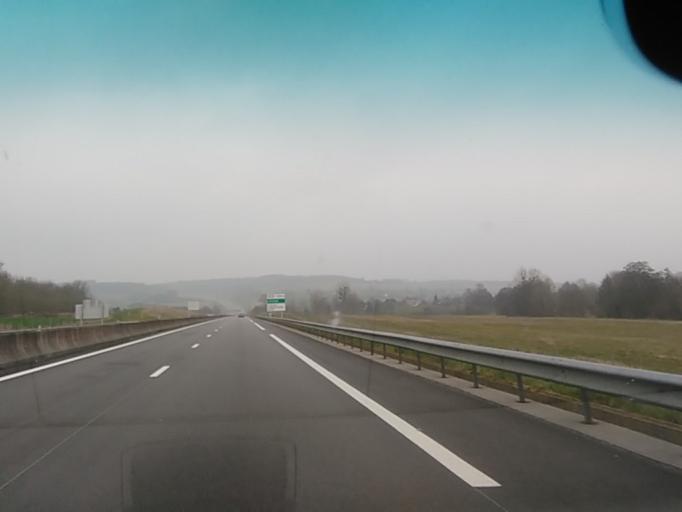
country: FR
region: Lower Normandy
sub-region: Departement de l'Orne
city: Gace
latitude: 48.7666
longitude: 0.2920
